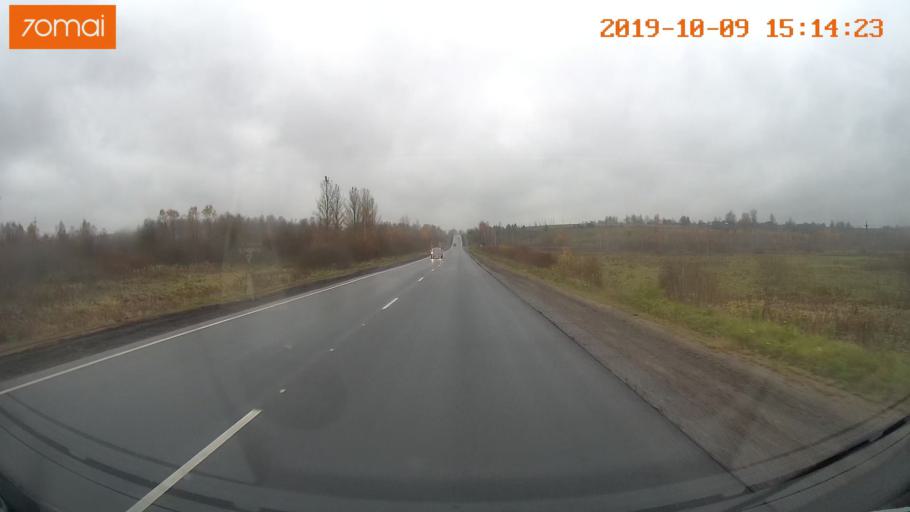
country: RU
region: Kostroma
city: Susanino
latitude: 58.1351
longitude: 41.6025
